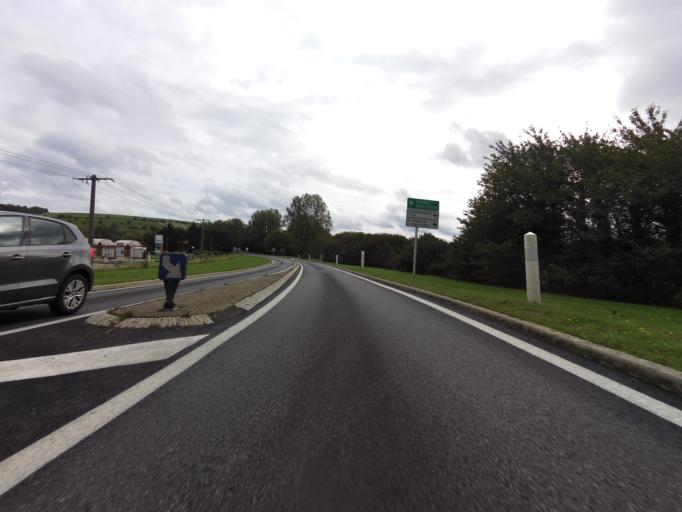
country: FR
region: Haute-Normandie
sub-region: Departement de la Seine-Maritime
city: Criel-sur-Mer
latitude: 50.0109
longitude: 1.3153
